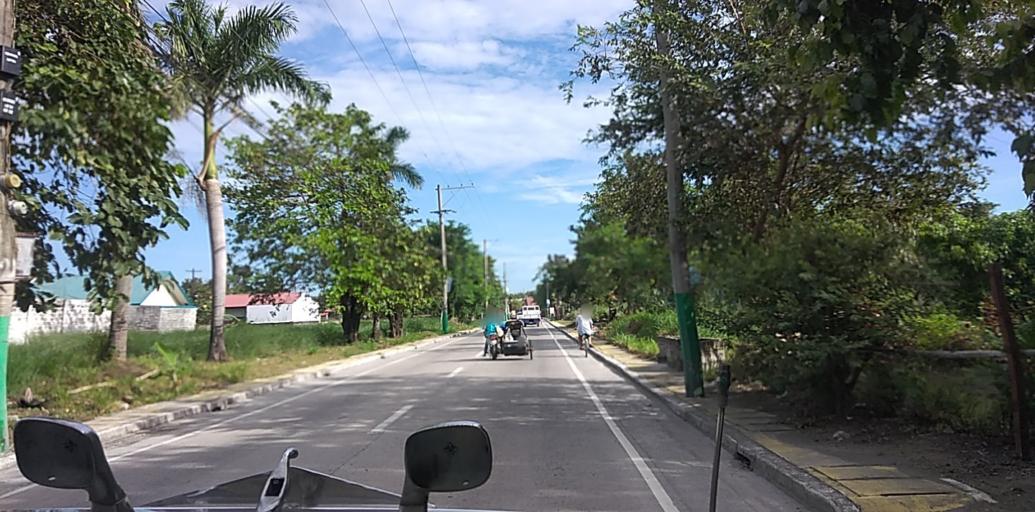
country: PH
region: Central Luzon
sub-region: Province of Pampanga
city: Malino
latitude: 15.1132
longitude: 120.6635
